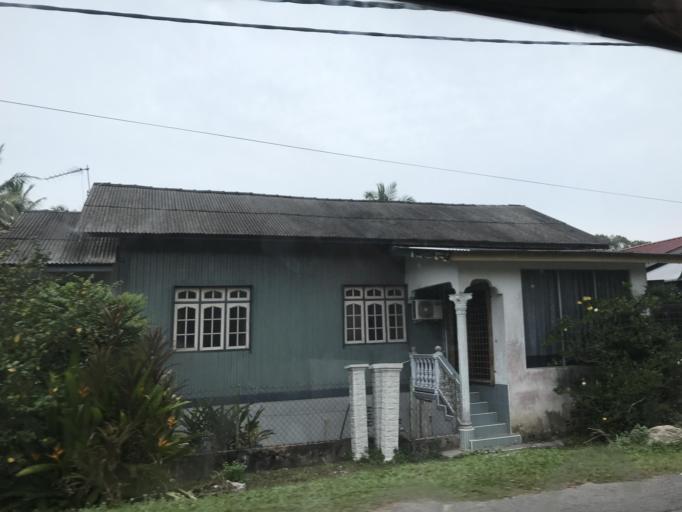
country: MY
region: Kelantan
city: Kota Bharu
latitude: 6.1759
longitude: 102.2196
